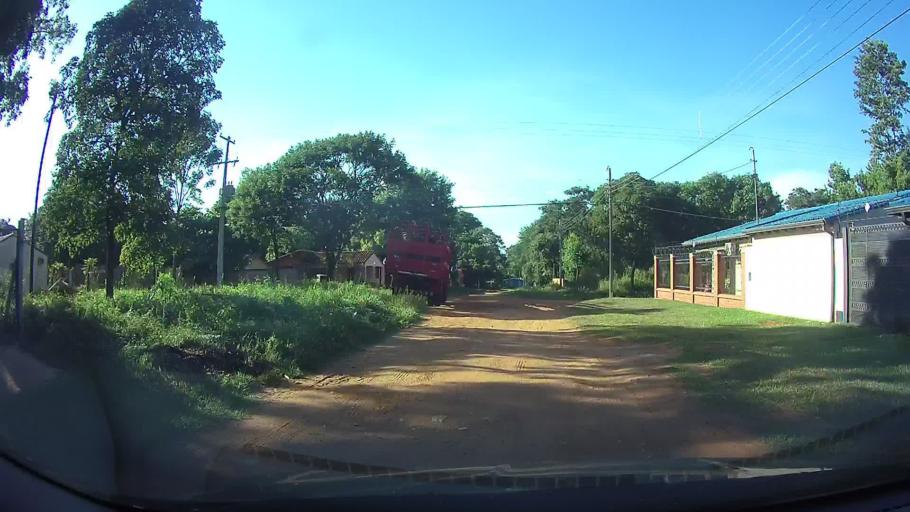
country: PY
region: Central
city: San Lorenzo
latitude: -25.2568
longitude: -57.4685
